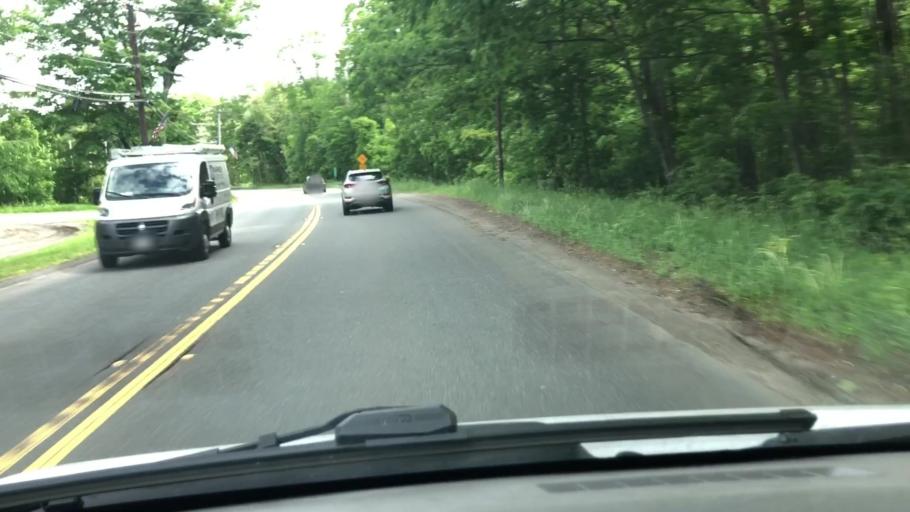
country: US
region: Massachusetts
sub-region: Hampshire County
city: Williamsburg
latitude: 42.3844
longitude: -72.7165
